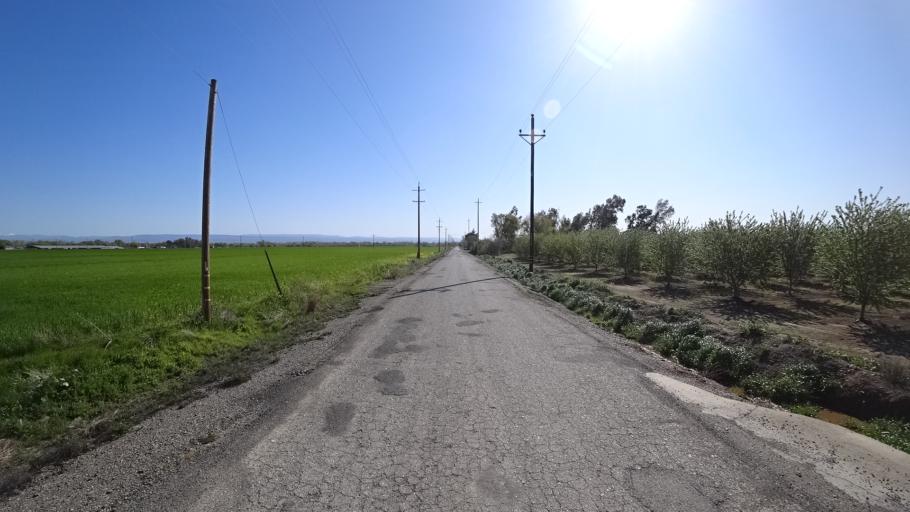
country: US
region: California
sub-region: Glenn County
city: Hamilton City
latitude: 39.7756
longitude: -122.0567
